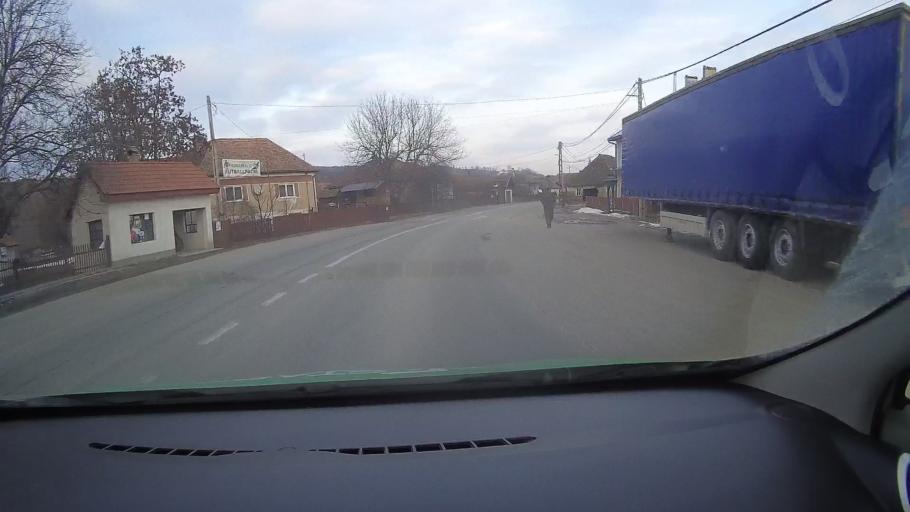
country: RO
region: Harghita
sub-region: Comuna Simonesti
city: Simonesti
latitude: 46.3572
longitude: 25.1424
